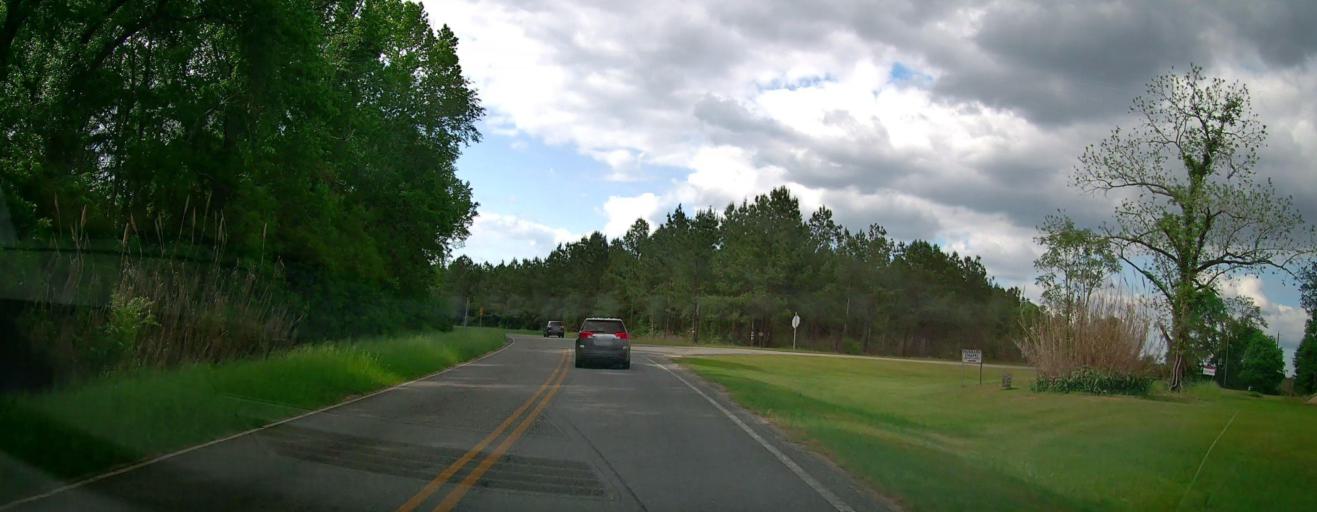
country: US
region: Georgia
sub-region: Laurens County
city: East Dublin
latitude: 32.7321
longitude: -82.9094
